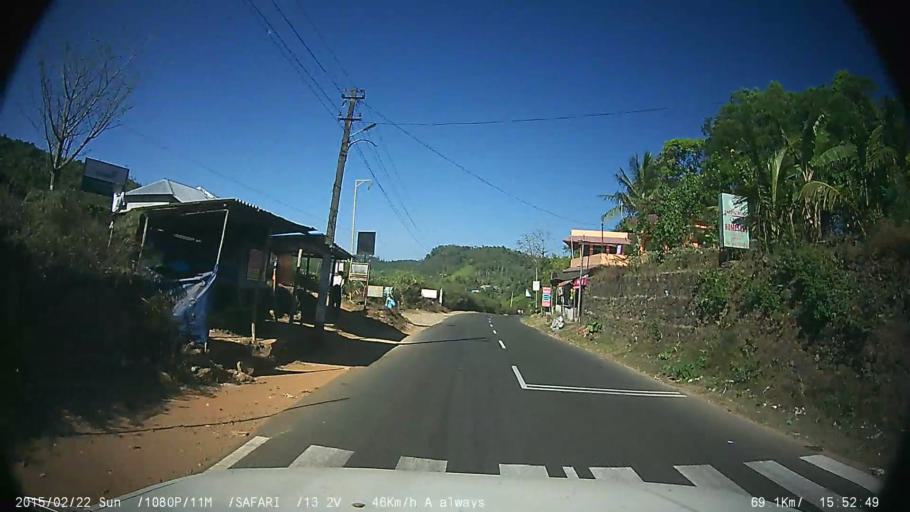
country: IN
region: Tamil Nadu
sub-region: Theni
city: Gudalur
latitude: 9.5744
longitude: 77.0117
